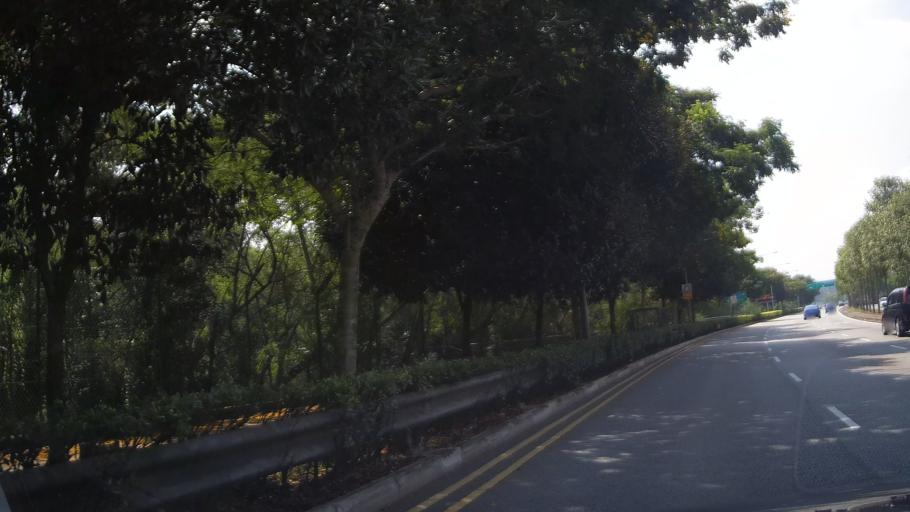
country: MY
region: Johor
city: Kampung Pasir Gudang Baru
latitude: 1.3785
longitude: 103.9084
